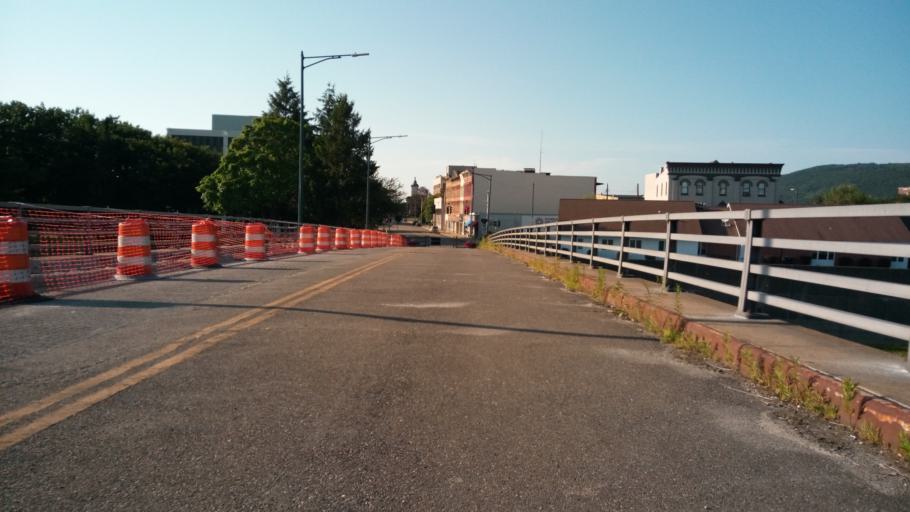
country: US
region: New York
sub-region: Chemung County
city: Elmira
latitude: 42.0875
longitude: -76.8007
